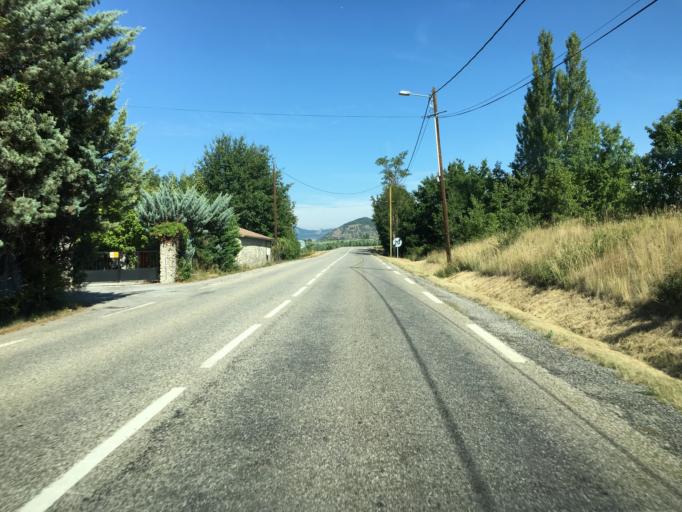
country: FR
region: Provence-Alpes-Cote d'Azur
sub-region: Departement des Hautes-Alpes
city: Laragne-Monteglin
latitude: 44.3525
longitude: 5.7664
